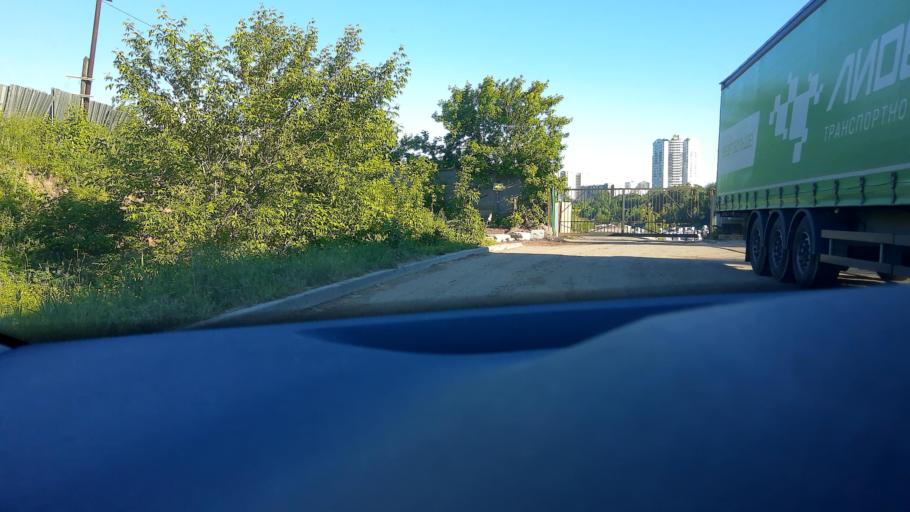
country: RU
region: Moscow
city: Khimki
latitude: 55.8788
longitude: 37.4396
